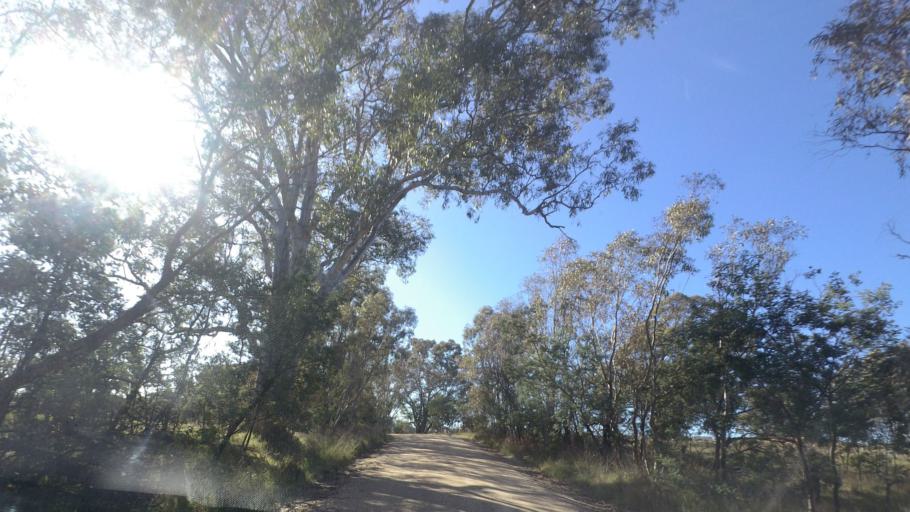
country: AU
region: Victoria
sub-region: Mount Alexander
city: Castlemaine
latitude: -37.1096
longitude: 144.4187
